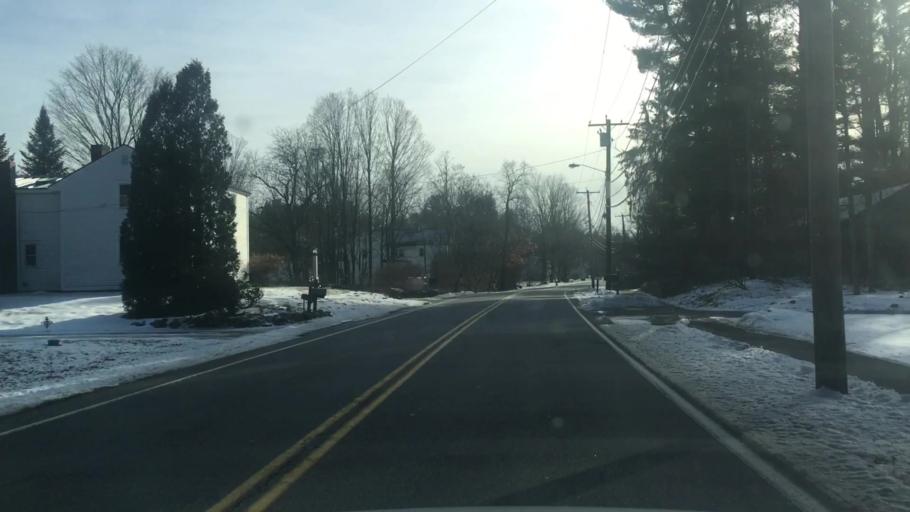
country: US
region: New Hampshire
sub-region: Merrimack County
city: East Concord
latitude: 43.2490
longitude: -71.5391
